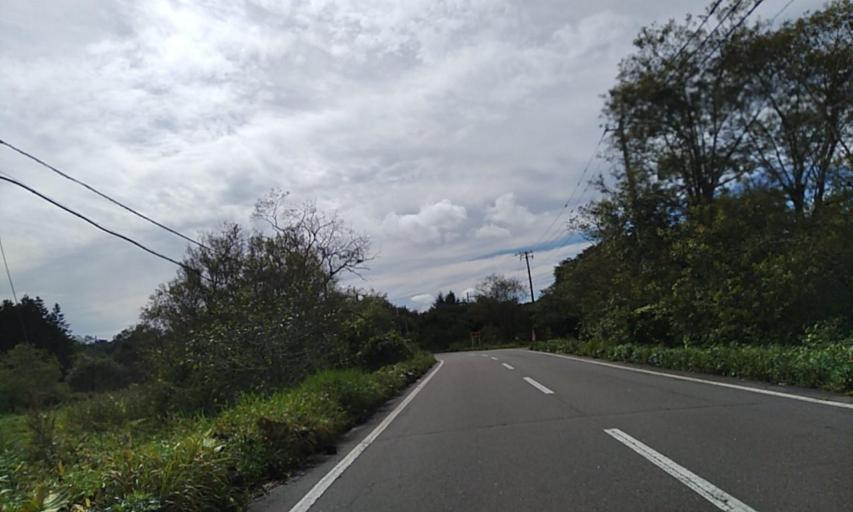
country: JP
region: Hokkaido
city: Kushiro
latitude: 42.8450
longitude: 143.8437
